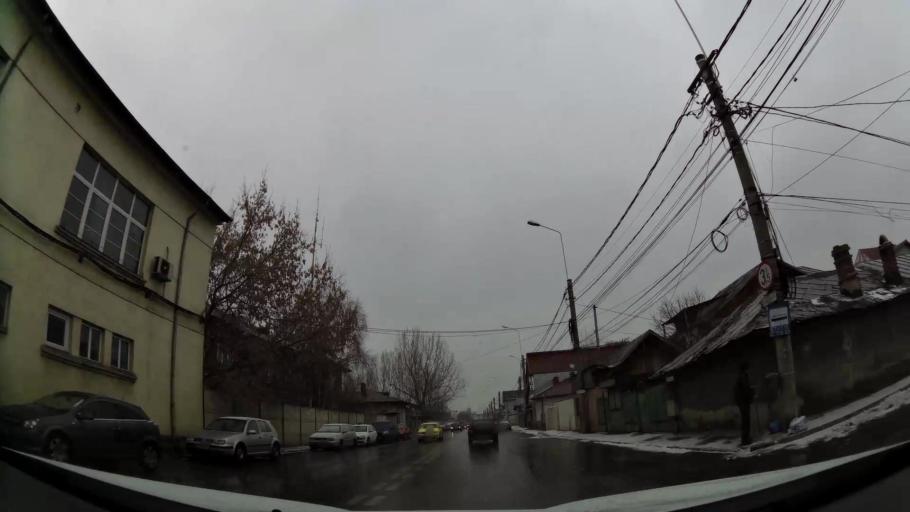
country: RO
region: Prahova
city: Ploiesti
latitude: 44.9556
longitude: 26.0150
